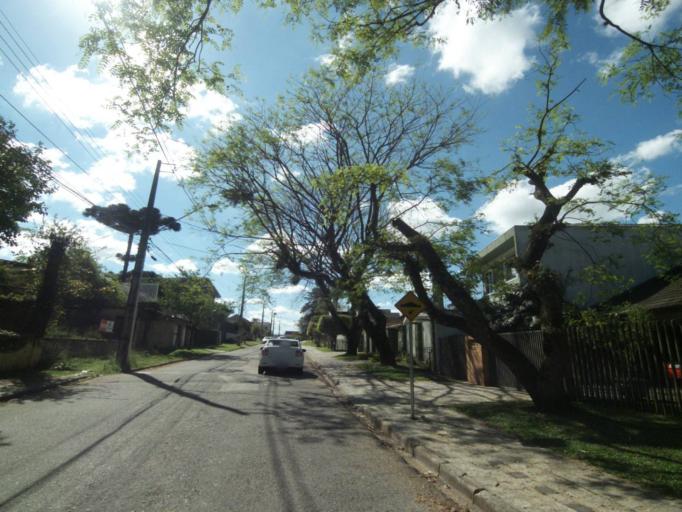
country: BR
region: Parana
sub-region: Curitiba
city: Curitiba
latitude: -25.3978
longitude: -49.2554
